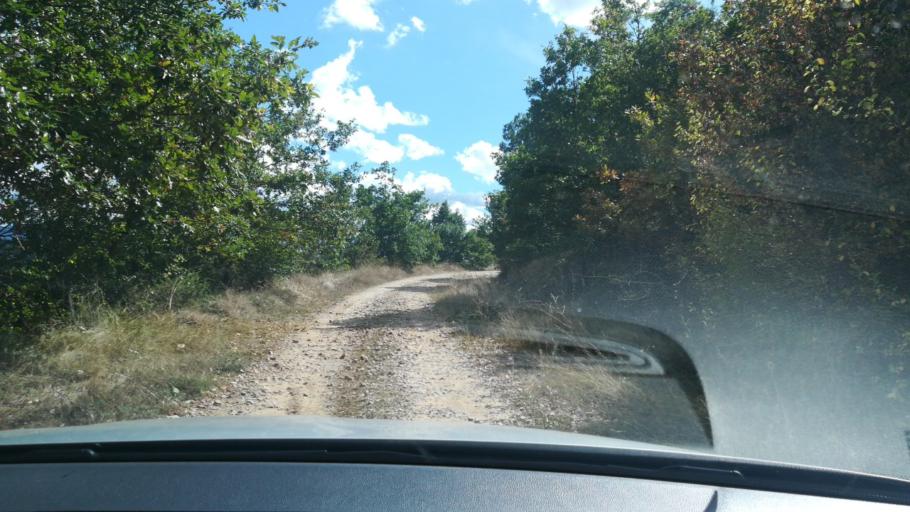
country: MK
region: Delcevo
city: Delcevo
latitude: 41.8963
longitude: 22.8056
